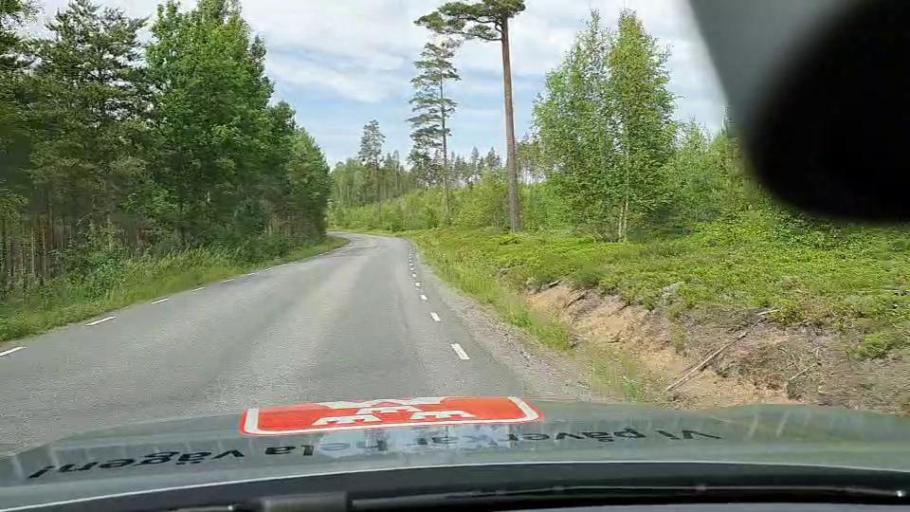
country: SE
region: Soedermanland
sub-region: Eskilstuna Kommun
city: Arla
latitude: 59.2450
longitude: 16.7180
